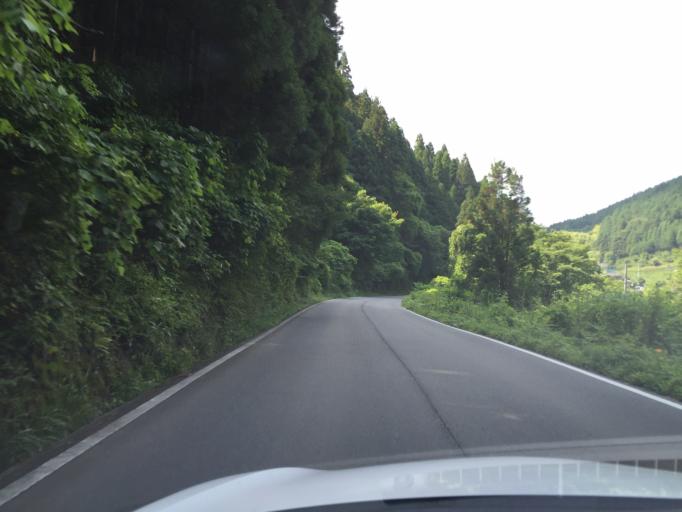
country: JP
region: Fukushima
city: Iwaki
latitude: 36.9990
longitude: 140.7106
